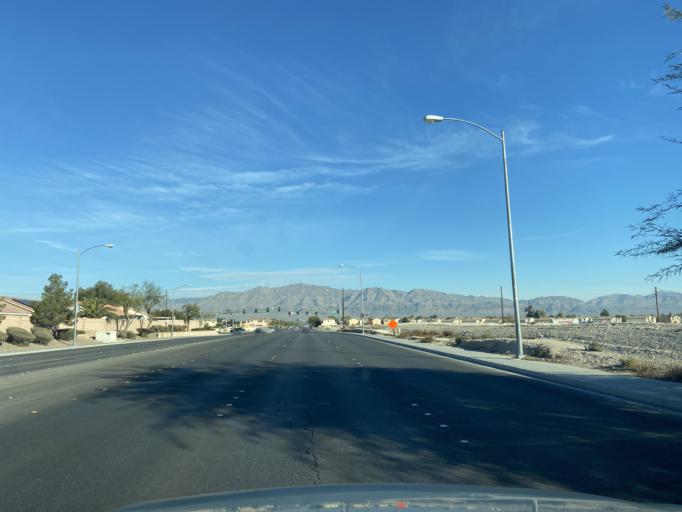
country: US
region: Nevada
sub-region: Clark County
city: North Las Vegas
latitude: 36.2452
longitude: -115.1800
